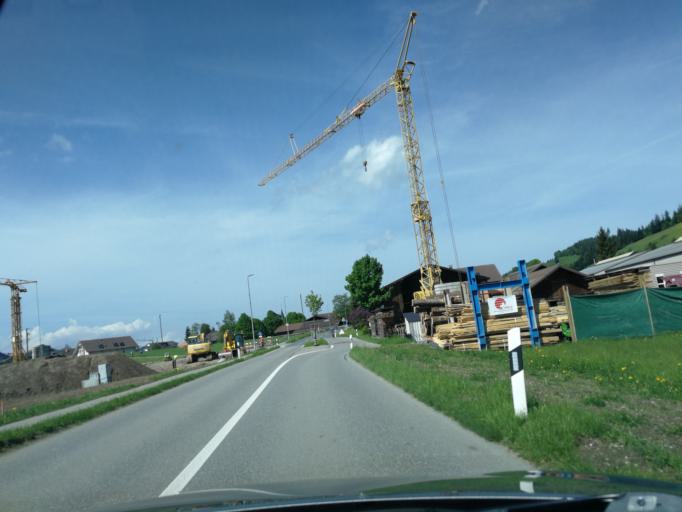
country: CH
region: Bern
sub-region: Bern-Mittelland District
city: Linden
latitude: 46.8480
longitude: 7.6821
